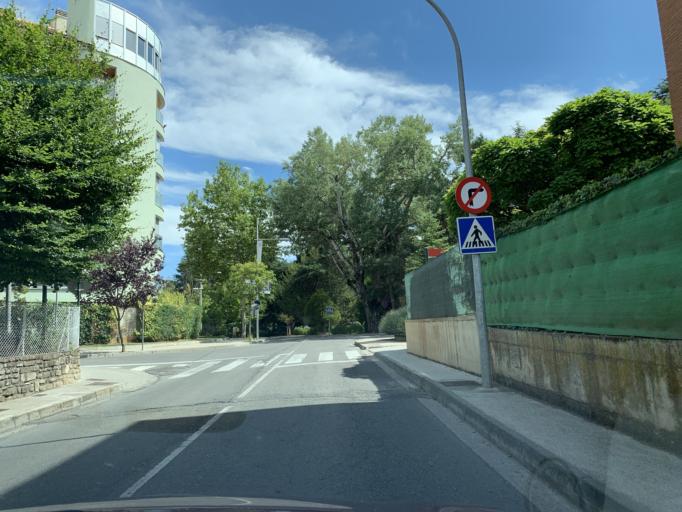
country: ES
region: Aragon
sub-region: Provincia de Huesca
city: Jaca
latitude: 42.5710
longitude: -0.5554
